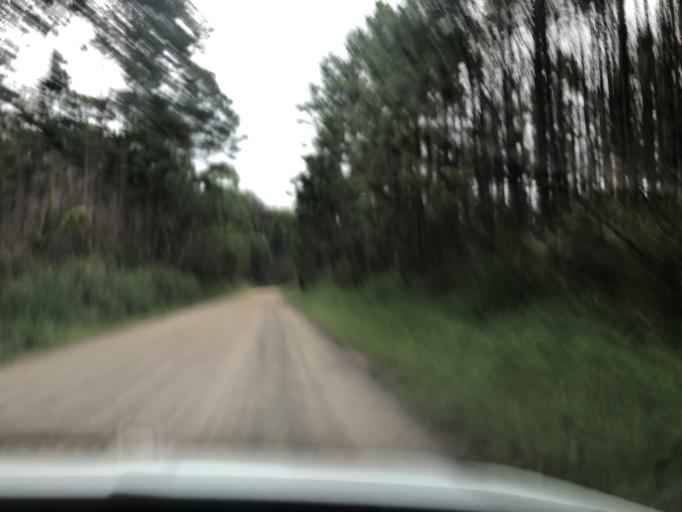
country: BR
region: Santa Catarina
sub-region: Florianopolis
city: Lagoa
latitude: -27.5480
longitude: -48.4422
